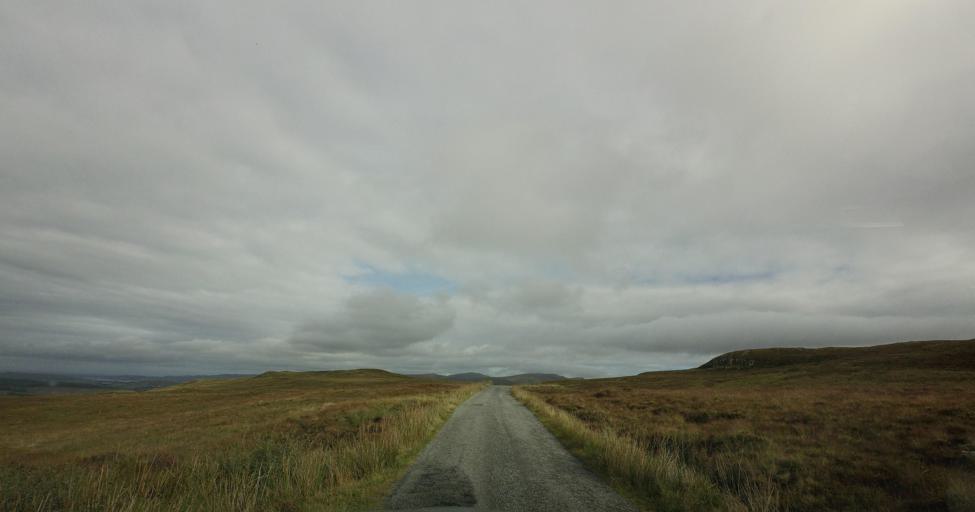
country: GB
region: Scotland
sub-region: Highland
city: Isle of Skye
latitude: 57.4071
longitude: -6.2657
